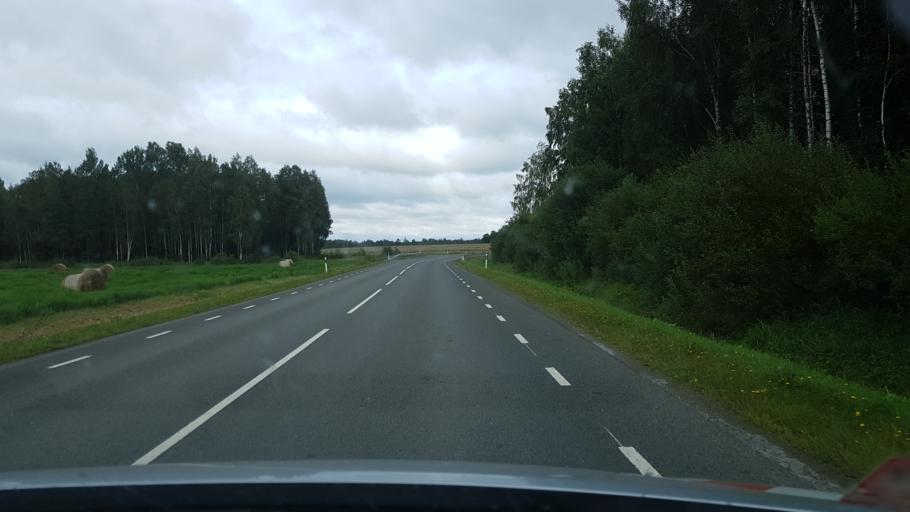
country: EE
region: Jogevamaa
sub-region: Poltsamaa linn
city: Poltsamaa
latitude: 58.5368
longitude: 25.9504
